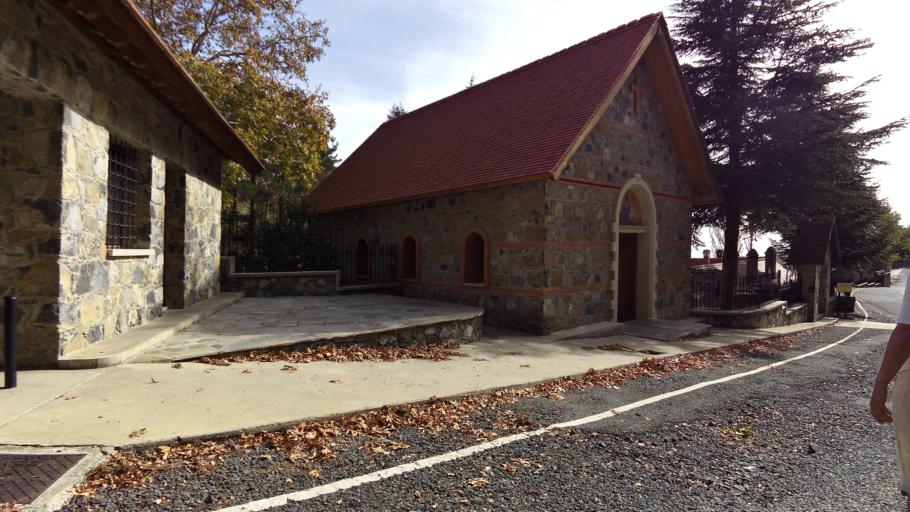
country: CY
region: Lefkosia
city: Kakopetria
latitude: 34.9134
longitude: 32.8381
